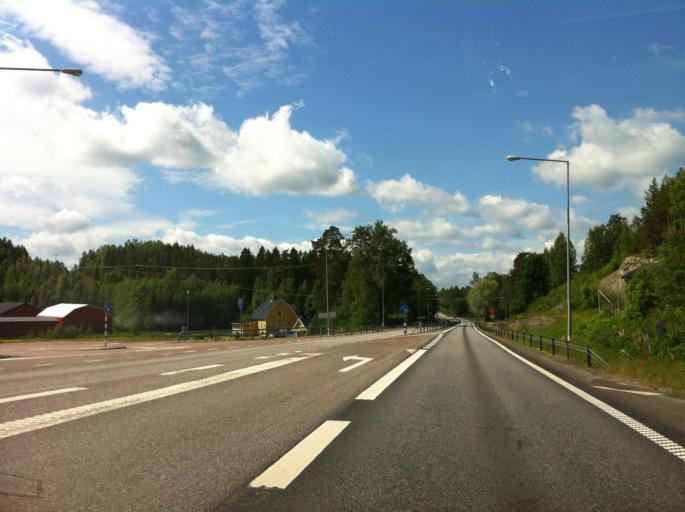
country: SE
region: Vaermland
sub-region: Grums Kommun
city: Slottsbron
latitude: 59.3165
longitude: 13.0997
